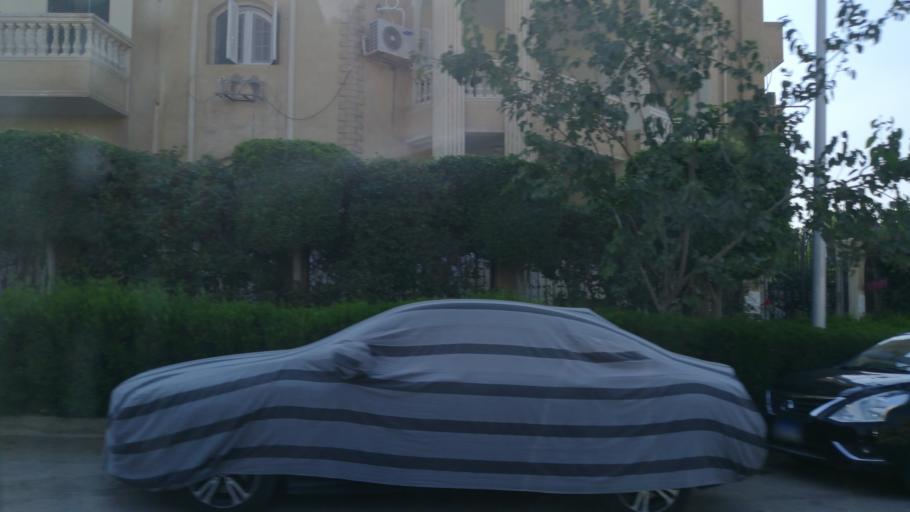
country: EG
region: Muhafazat al Qahirah
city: Cairo
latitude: 30.0143
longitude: 31.4212
